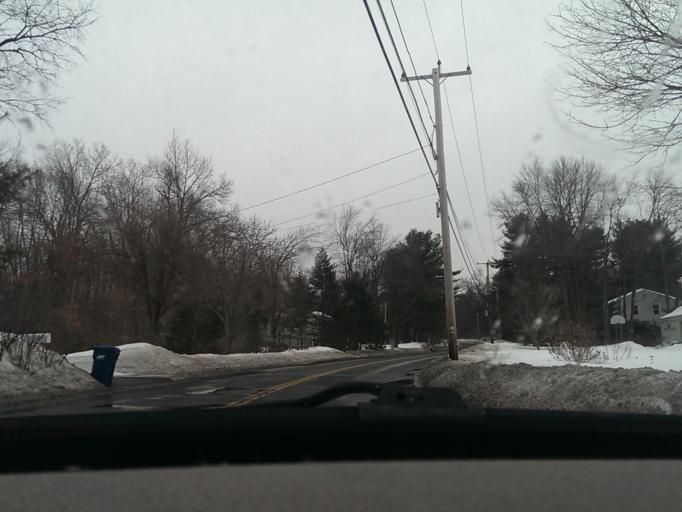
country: US
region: Massachusetts
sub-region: Hampden County
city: Wilbraham
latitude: 42.0946
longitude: -72.4464
